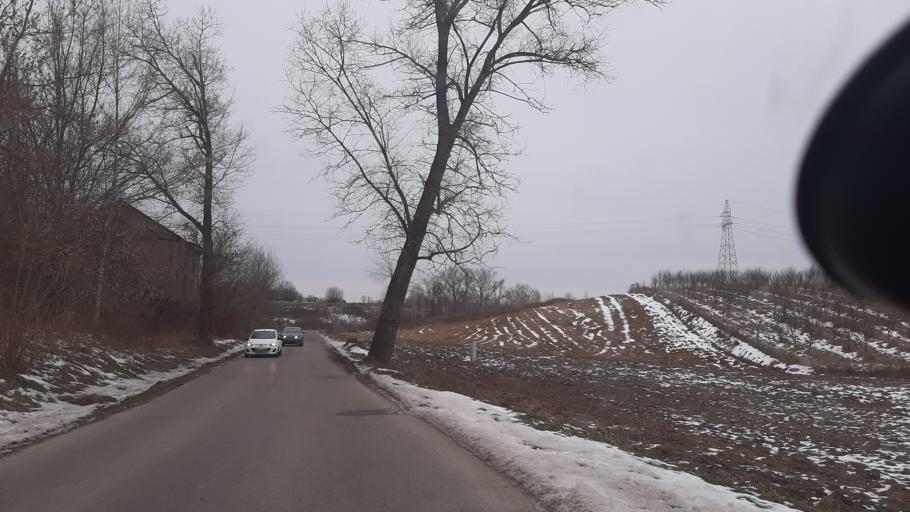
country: PL
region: Lublin Voivodeship
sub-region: Powiat lubelski
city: Jakubowice Murowane
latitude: 51.2827
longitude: 22.6107
